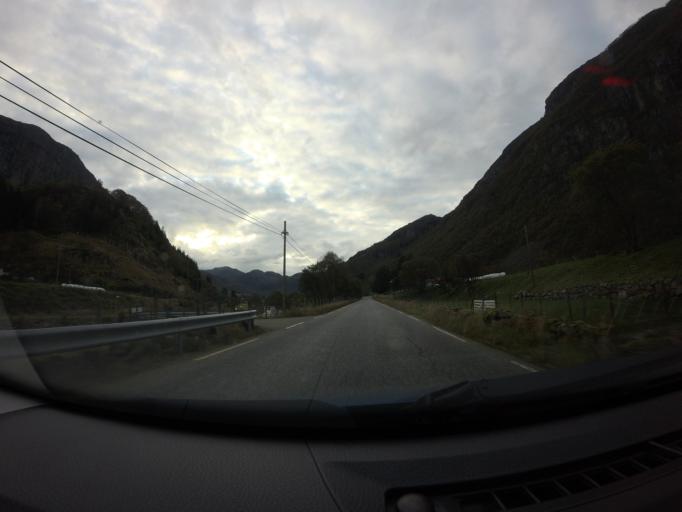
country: NO
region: Rogaland
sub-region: Forsand
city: Forsand
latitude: 58.8113
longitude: 6.2320
